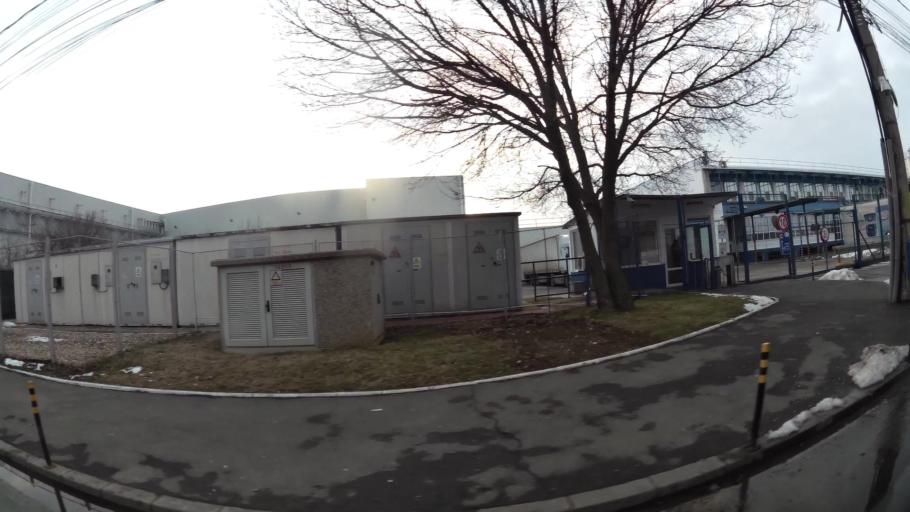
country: RO
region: Ilfov
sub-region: Comuna Fundeni-Dobroesti
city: Fundeni
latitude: 44.4696
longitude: 26.1649
